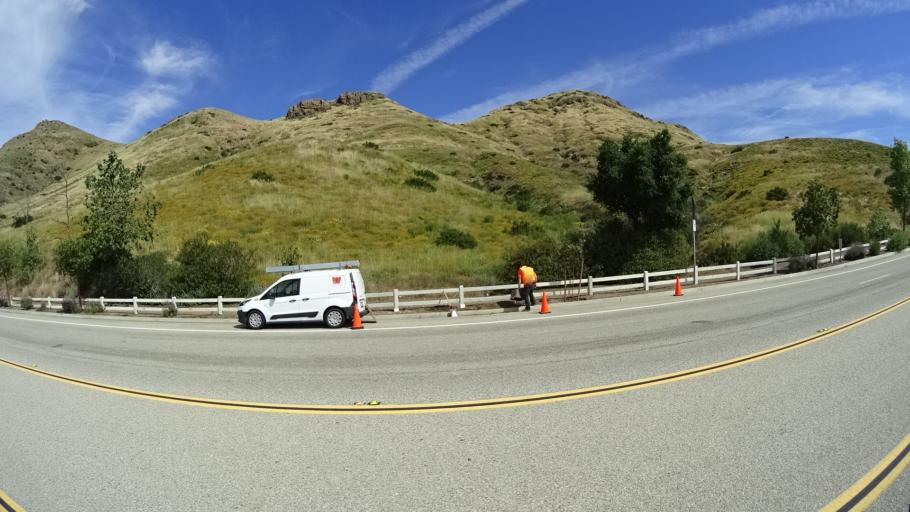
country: US
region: California
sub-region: Ventura County
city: Casa Conejo
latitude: 34.1803
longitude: -118.9719
